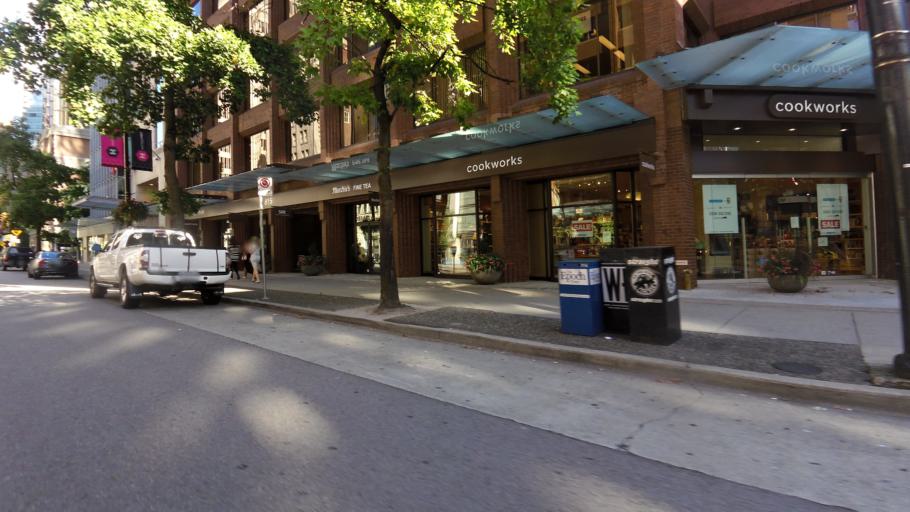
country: CA
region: British Columbia
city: West End
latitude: 49.2860
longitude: -123.1150
